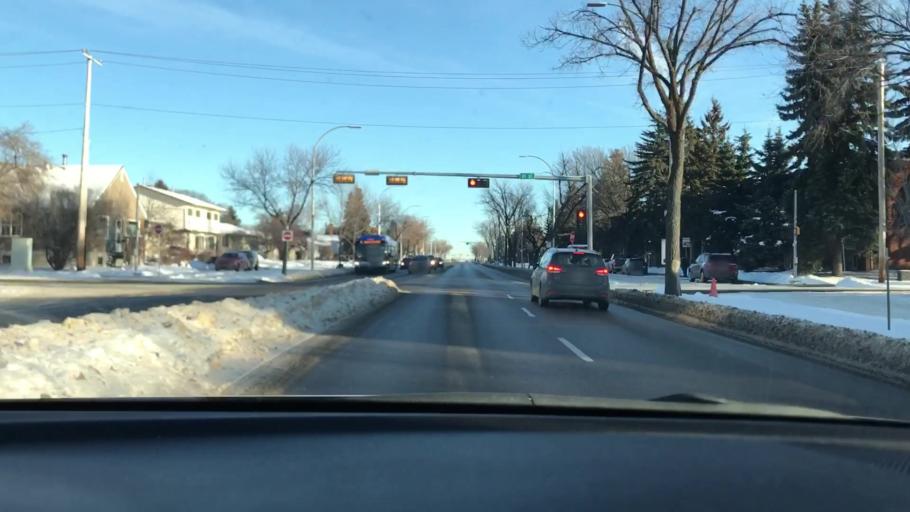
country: CA
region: Alberta
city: Edmonton
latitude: 53.5181
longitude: -113.4523
